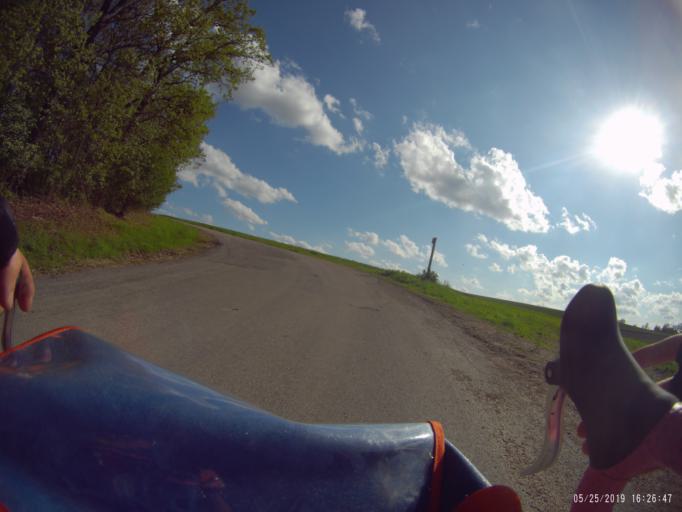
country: US
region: Wisconsin
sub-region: Dane County
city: Mount Horeb
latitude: 42.9508
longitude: -89.7063
